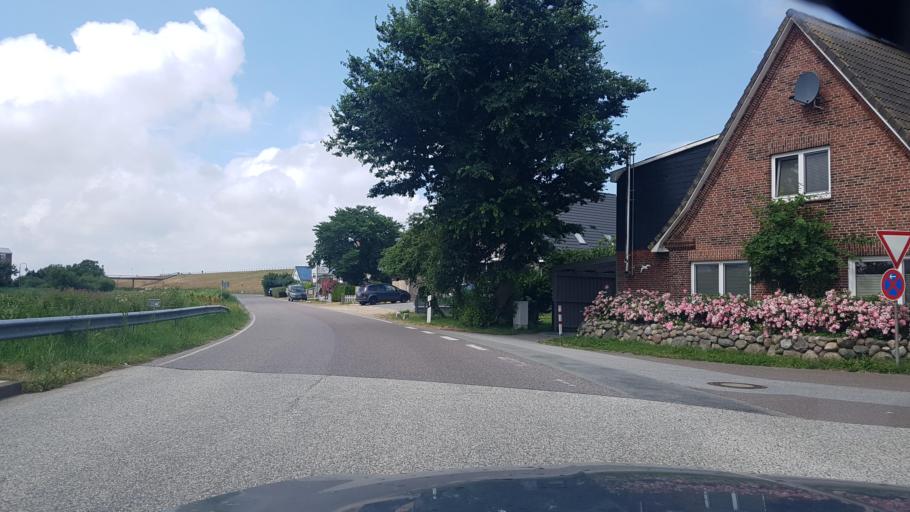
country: DE
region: Schleswig-Holstein
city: Elisabeth-Sophien-Koog
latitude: 54.5062
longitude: 8.8280
